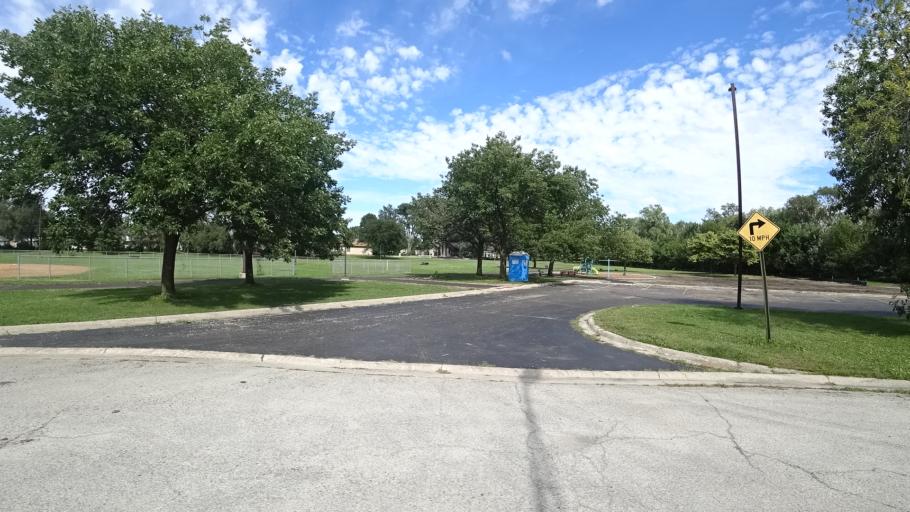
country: US
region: Illinois
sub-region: Cook County
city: Chicago Ridge
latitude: 41.7105
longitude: -87.7722
